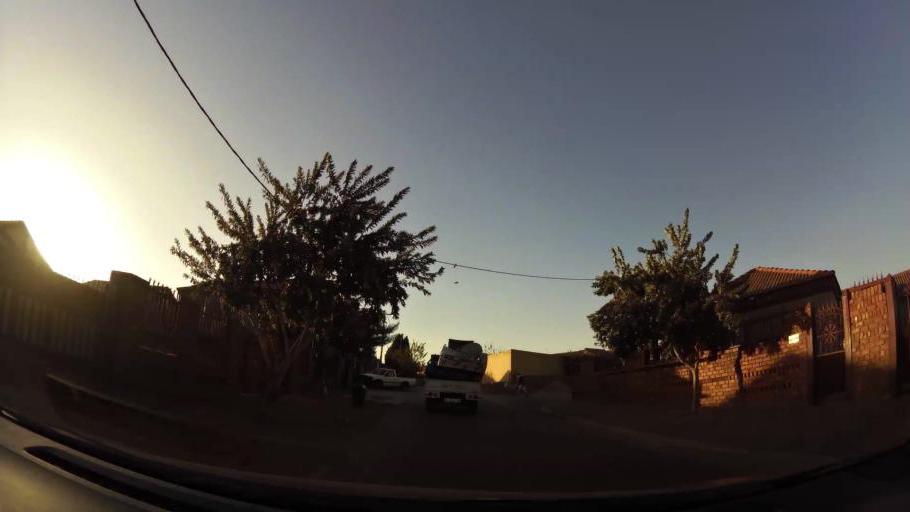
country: ZA
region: Gauteng
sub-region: City of Tshwane Metropolitan Municipality
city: Mabopane
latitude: -25.5833
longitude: 28.1027
